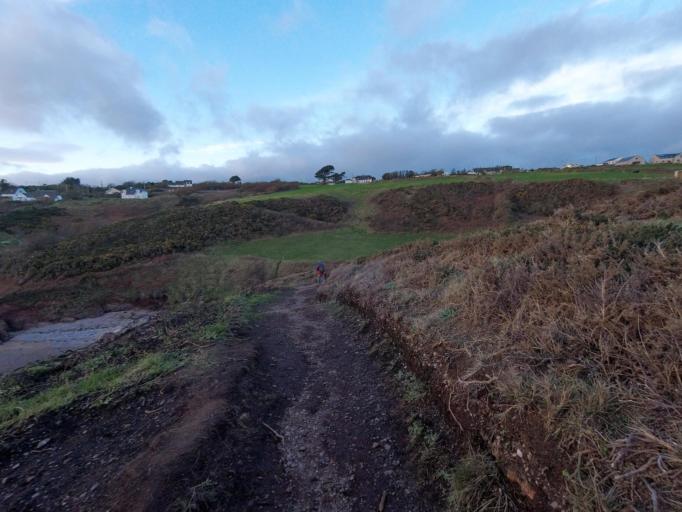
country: IE
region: Munster
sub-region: Waterford
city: Dunmore East
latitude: 52.1396
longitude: -7.0152
